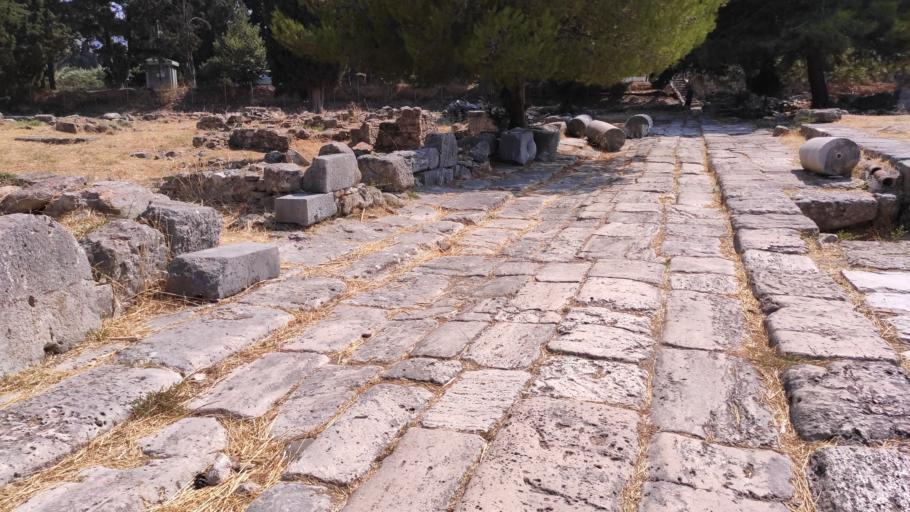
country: GR
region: South Aegean
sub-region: Nomos Dodekanisou
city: Kos
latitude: 36.8908
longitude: 27.2847
